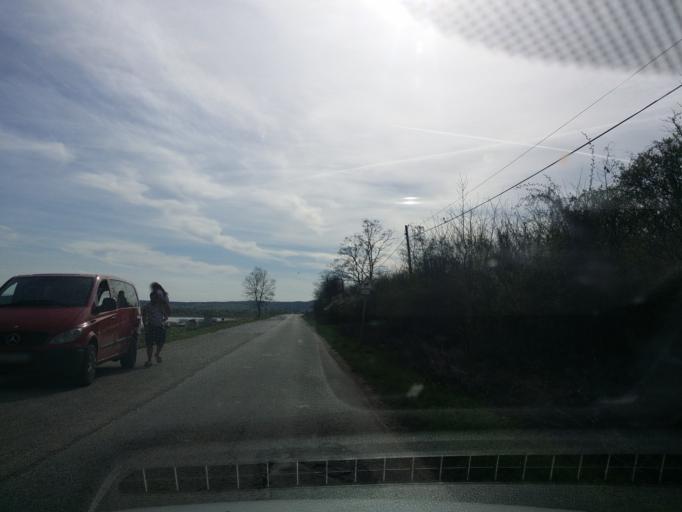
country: HU
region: Borsod-Abauj-Zemplen
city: Szendro
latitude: 48.4530
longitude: 20.7675
